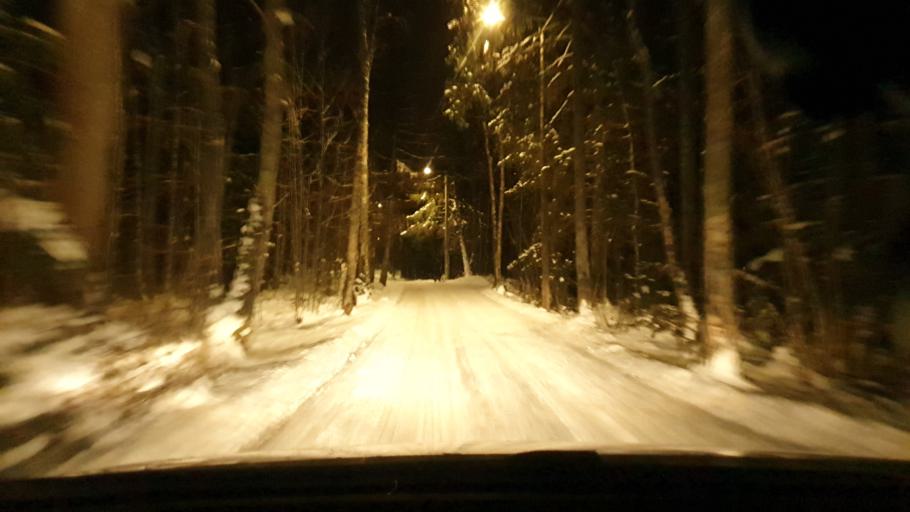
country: EE
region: Harju
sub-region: Viimsi vald
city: Viimsi
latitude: 59.5187
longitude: 24.9049
